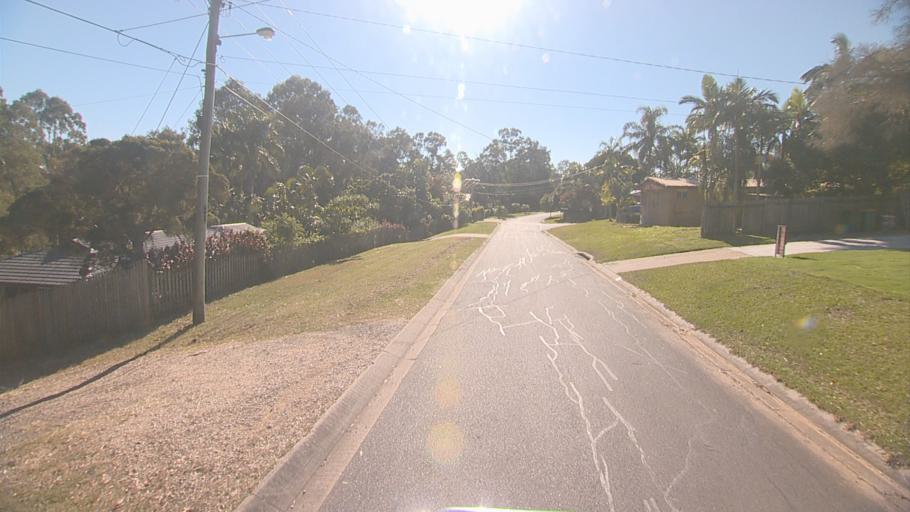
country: AU
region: Queensland
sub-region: Logan
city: Slacks Creek
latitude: -27.6523
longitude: 153.1542
